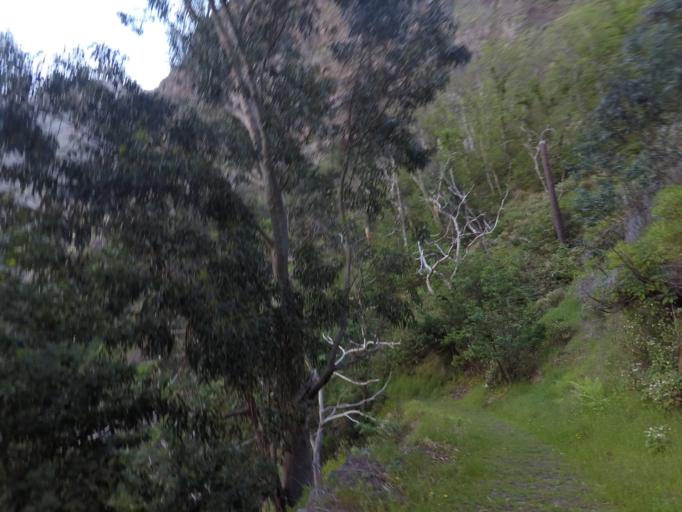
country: PT
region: Madeira
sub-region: Camara de Lobos
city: Curral das Freiras
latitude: 32.7138
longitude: -16.9653
